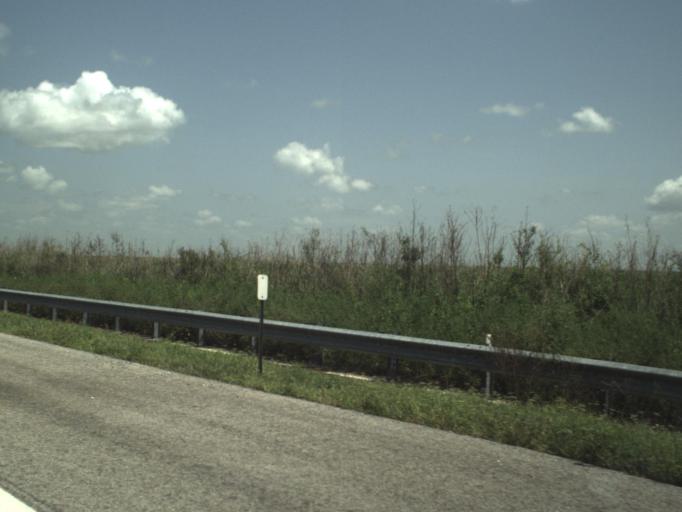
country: US
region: Florida
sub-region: Palm Beach County
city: Belle Glade Camp
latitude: 26.3889
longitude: -80.5794
